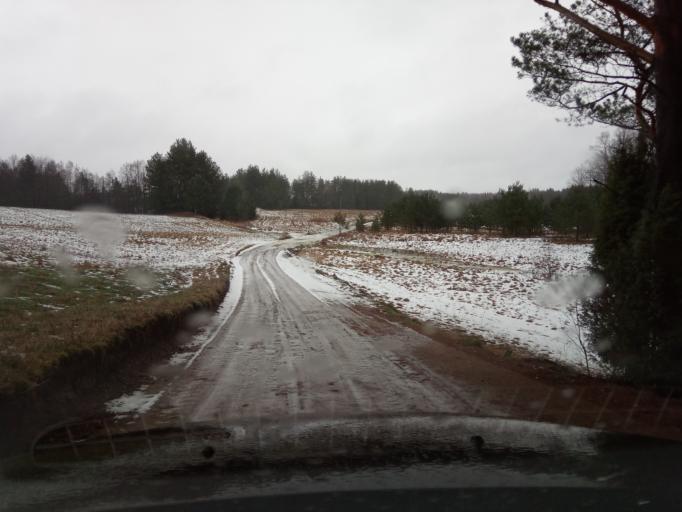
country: LT
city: Svencioneliai
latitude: 55.3373
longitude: 25.8073
